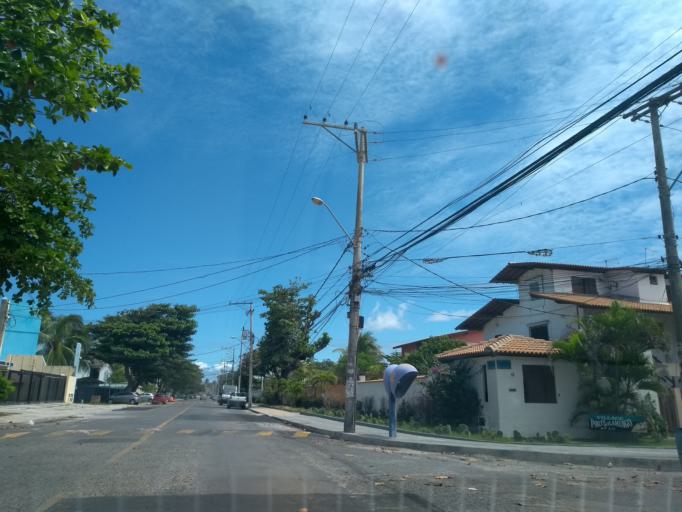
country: BR
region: Bahia
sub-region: Lauro De Freitas
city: Lauro de Freitas
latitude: -12.9315
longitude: -38.3232
